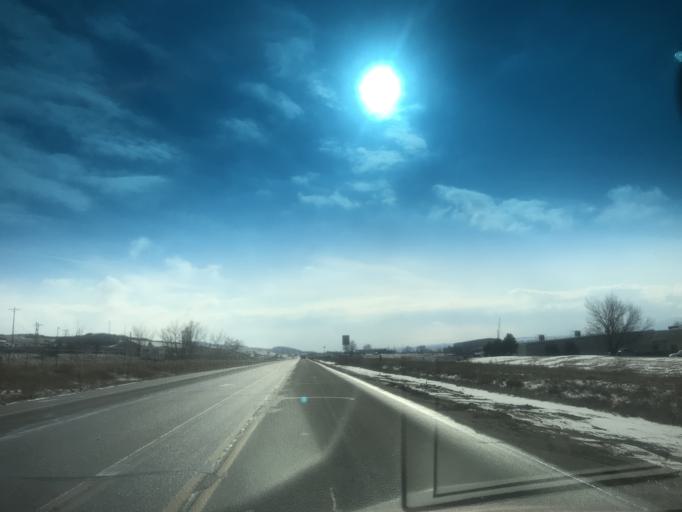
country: US
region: Colorado
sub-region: Douglas County
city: Highlands Ranch
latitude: 39.4812
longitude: -104.9938
